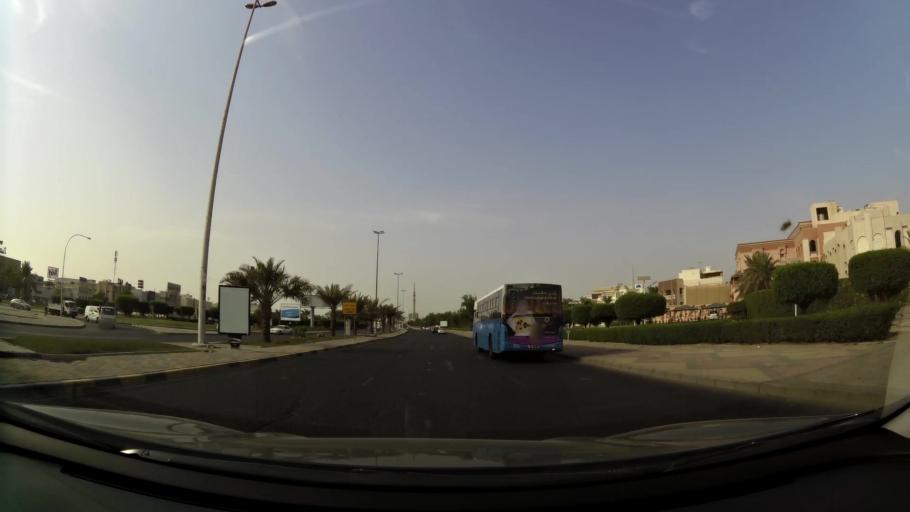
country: KW
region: Al Asimah
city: Ash Shamiyah
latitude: 29.3295
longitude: 47.9550
